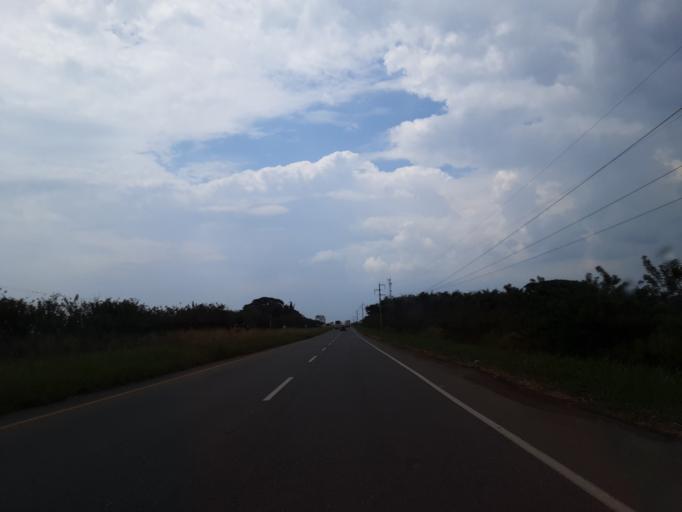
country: CO
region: Cauca
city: Caloto
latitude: 3.1106
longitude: -76.4672
